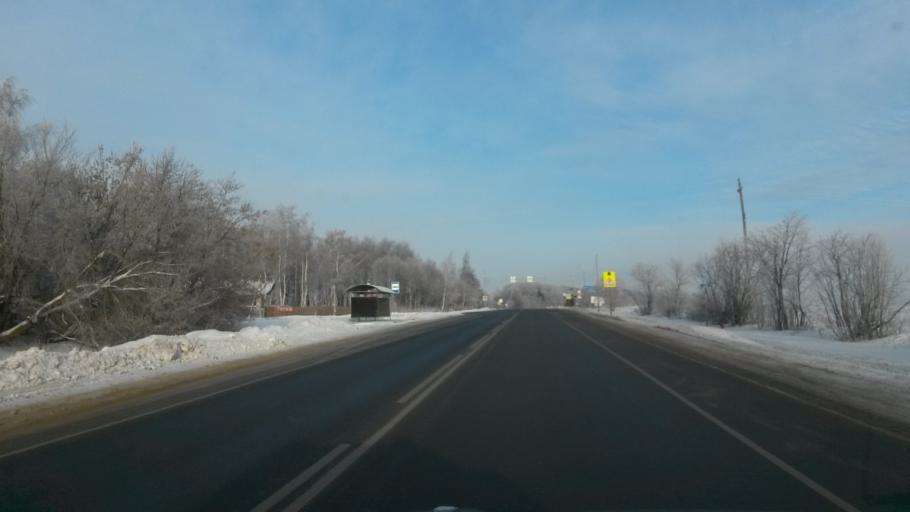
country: RU
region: Vladimir
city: Bogolyubovo
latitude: 56.2196
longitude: 40.4415
